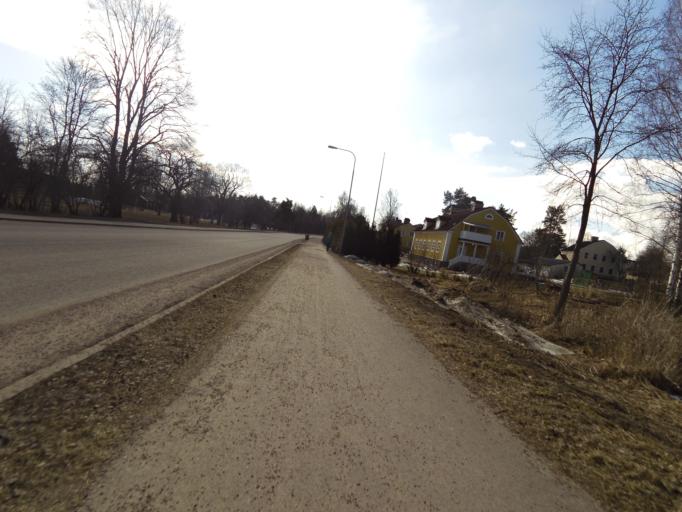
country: SE
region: Gaevleborg
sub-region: Hofors Kommun
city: Hofors
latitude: 60.5488
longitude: 16.2918
